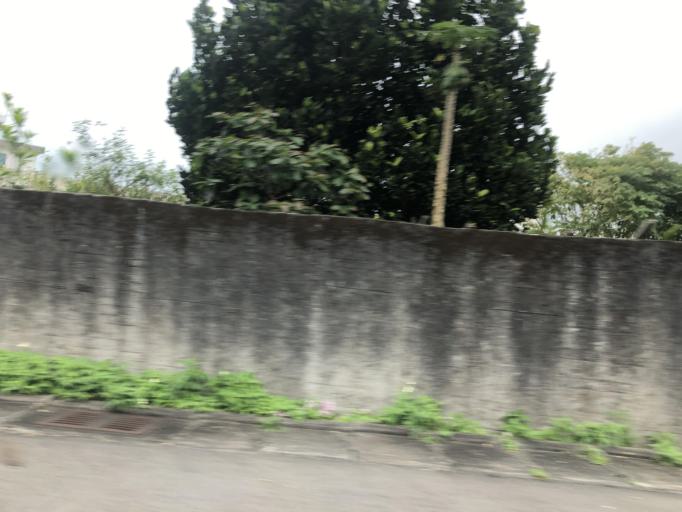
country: TW
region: Taiwan
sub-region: Keelung
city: Keelung
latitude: 25.2160
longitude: 121.6478
